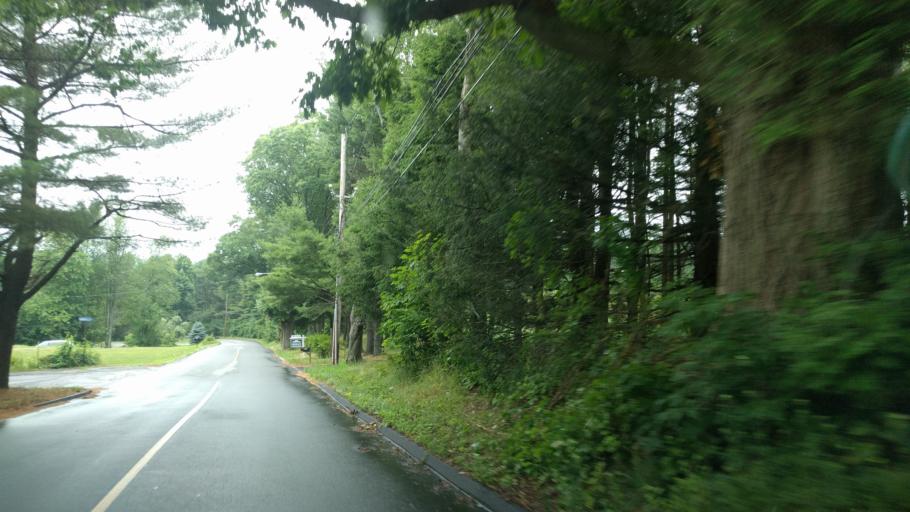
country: US
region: Massachusetts
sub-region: Worcester County
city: Auburn
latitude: 42.1939
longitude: -71.8190
